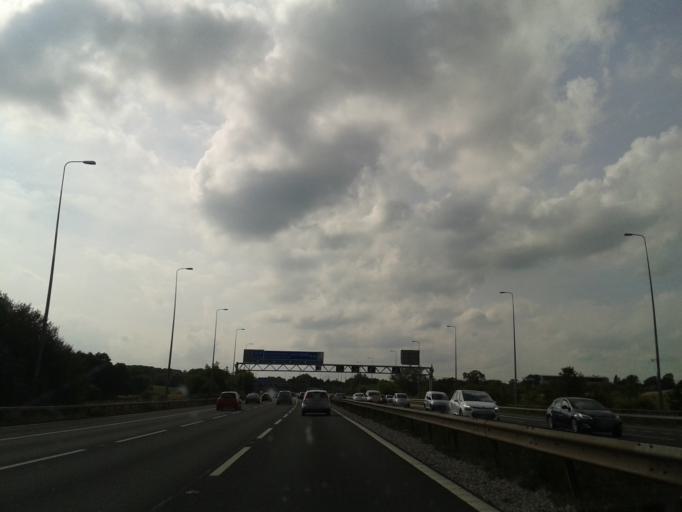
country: GB
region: England
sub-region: Solihull
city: Solihull
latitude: 52.3852
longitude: -1.7813
